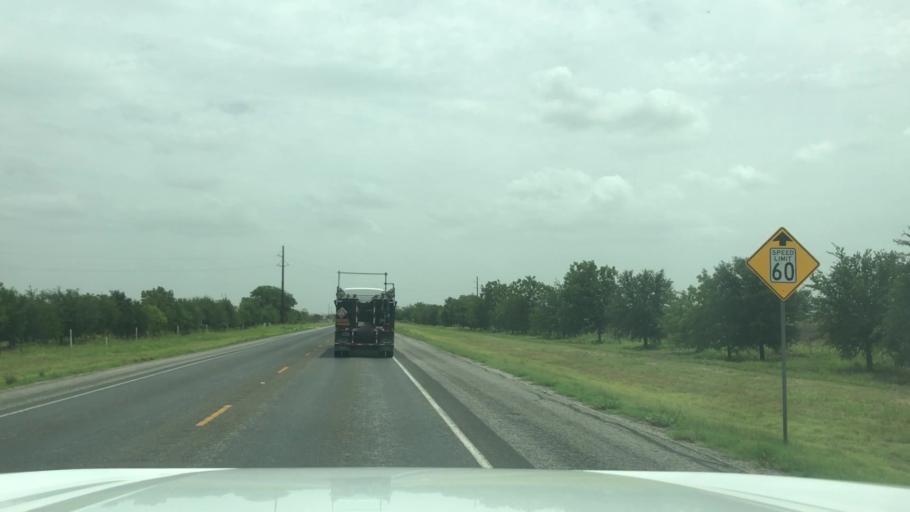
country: US
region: Texas
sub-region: Bosque County
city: Clifton
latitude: 31.7998
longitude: -97.5969
